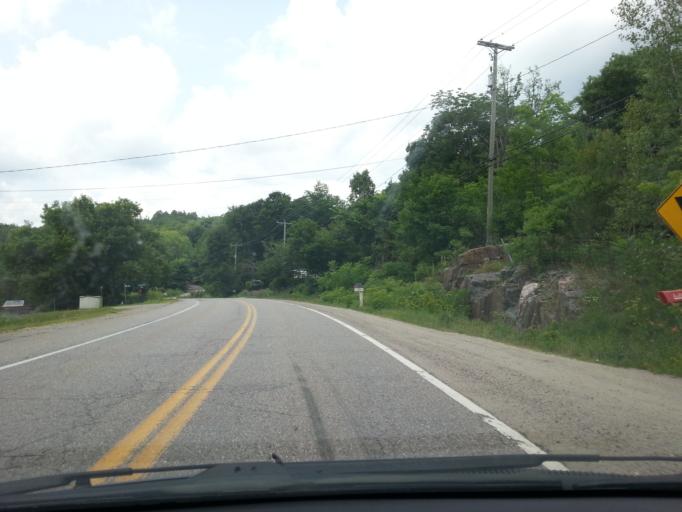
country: CA
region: Quebec
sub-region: Outaouais
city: Val-des-Monts
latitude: 45.6577
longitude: -75.6463
